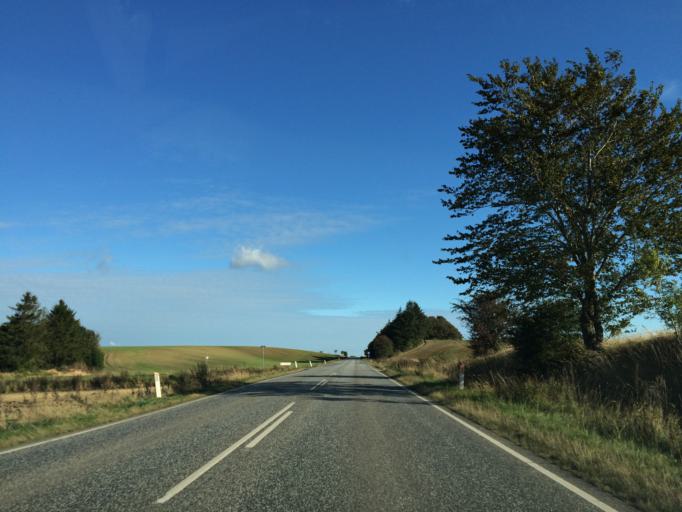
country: DK
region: Central Jutland
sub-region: Randers Kommune
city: Langa
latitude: 56.3822
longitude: 9.9573
